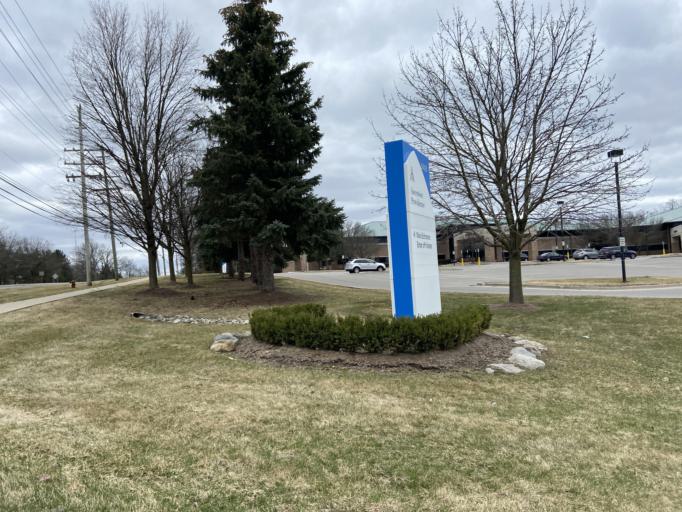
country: US
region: Michigan
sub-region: Oakland County
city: Franklin
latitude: 42.5070
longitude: -83.3202
